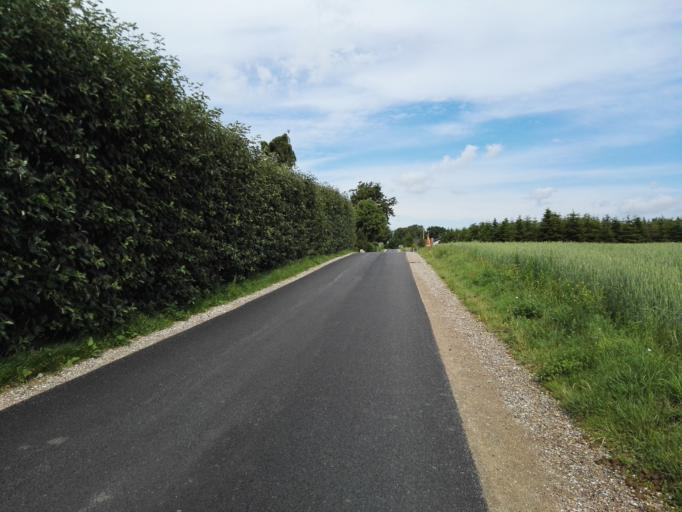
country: DK
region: Capital Region
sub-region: Egedal Kommune
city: Olstykke
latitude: 55.8135
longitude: 12.1765
